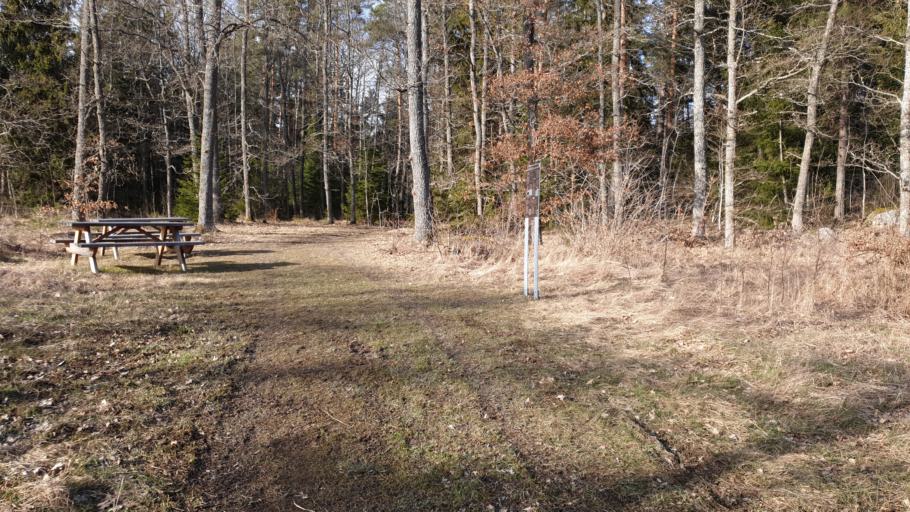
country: SE
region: Uppsala
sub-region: Enkopings Kommun
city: Grillby
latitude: 59.5974
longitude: 17.1621
